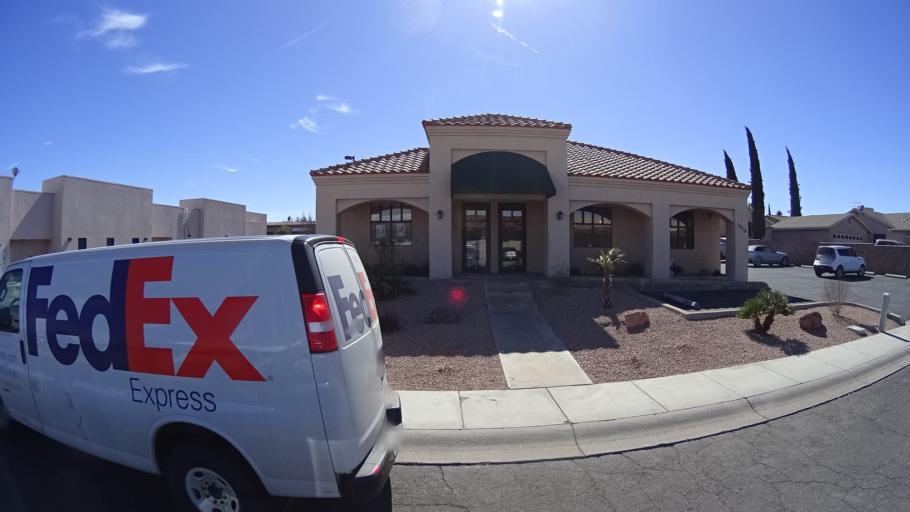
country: US
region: Arizona
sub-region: Mohave County
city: Kingman
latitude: 35.2096
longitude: -114.0358
